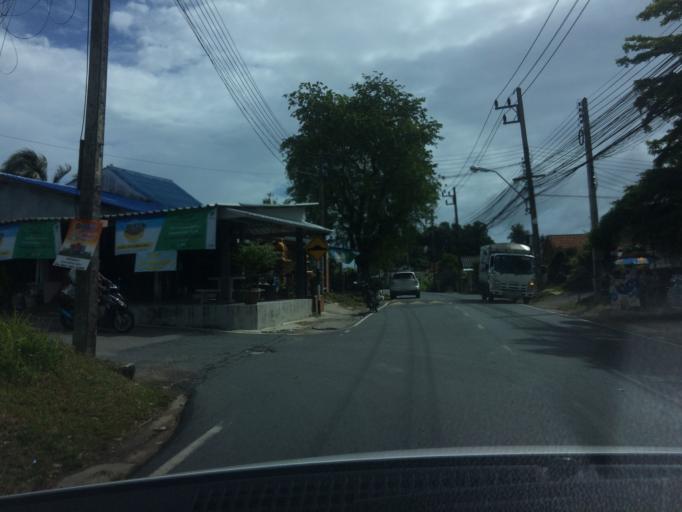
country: TH
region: Phuket
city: Thalang
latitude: 8.0290
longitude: 98.3385
